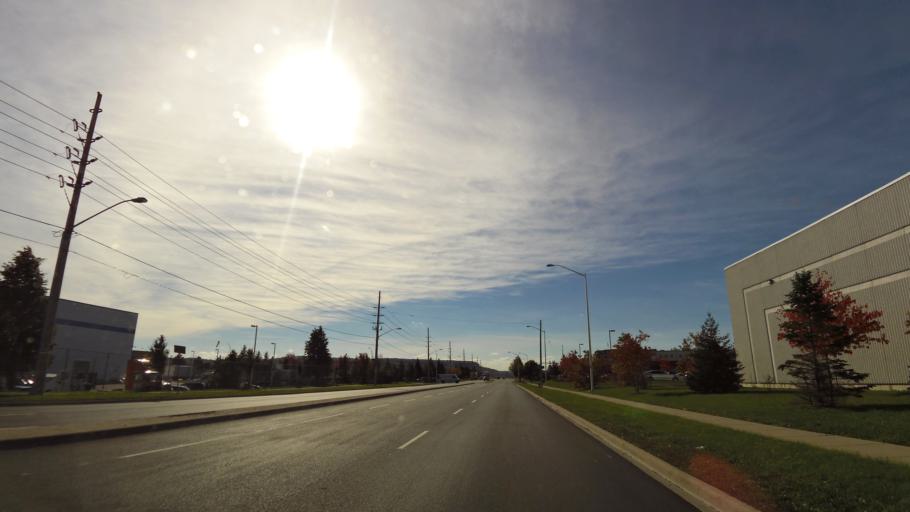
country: CA
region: Ontario
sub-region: Halton
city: Milton
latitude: 43.5372
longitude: -79.9101
